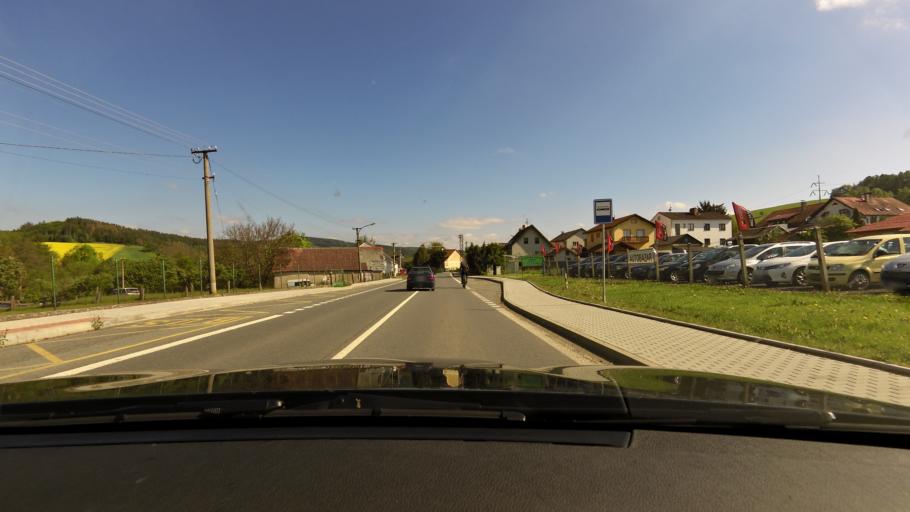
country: CZ
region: Plzensky
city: Klatovy
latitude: 49.3448
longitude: 13.2969
